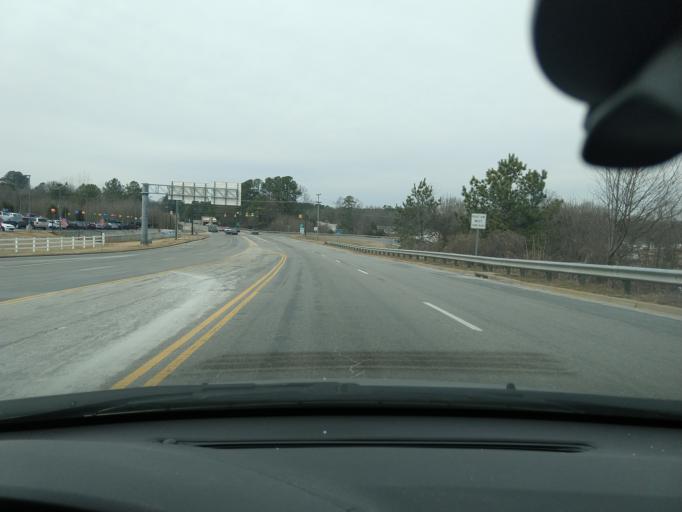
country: US
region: South Carolina
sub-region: Cherokee County
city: Gaffney
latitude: 35.0987
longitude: -81.6701
